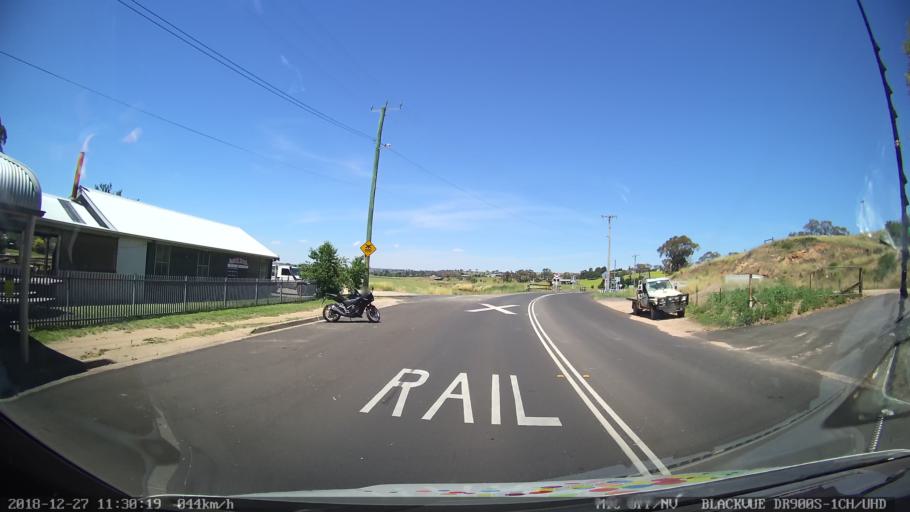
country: AU
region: New South Wales
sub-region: Bathurst Regional
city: Perthville
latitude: -33.4869
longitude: 149.5466
